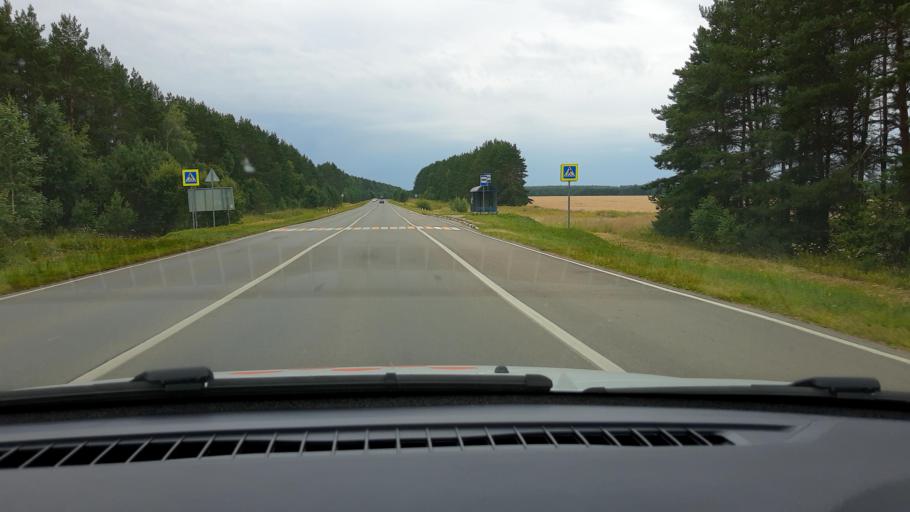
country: RU
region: Nizjnij Novgorod
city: Vyyezdnoye
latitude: 55.1715
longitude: 43.5951
